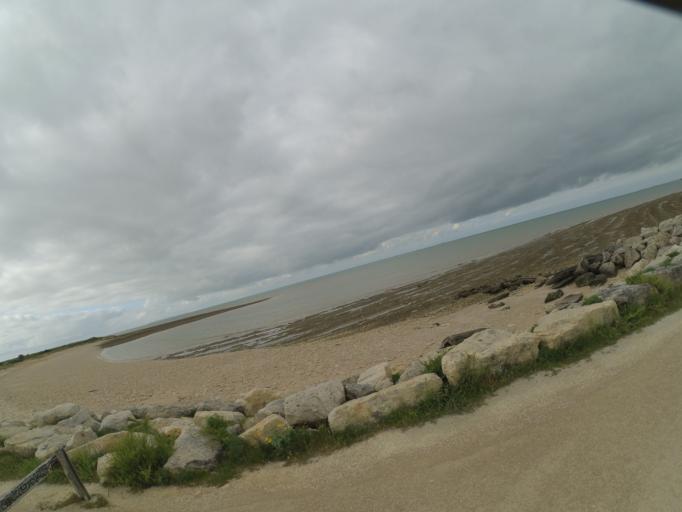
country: FR
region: Poitou-Charentes
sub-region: Departement de la Charente-Maritime
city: La Rochelle
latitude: 46.1334
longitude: -1.1495
